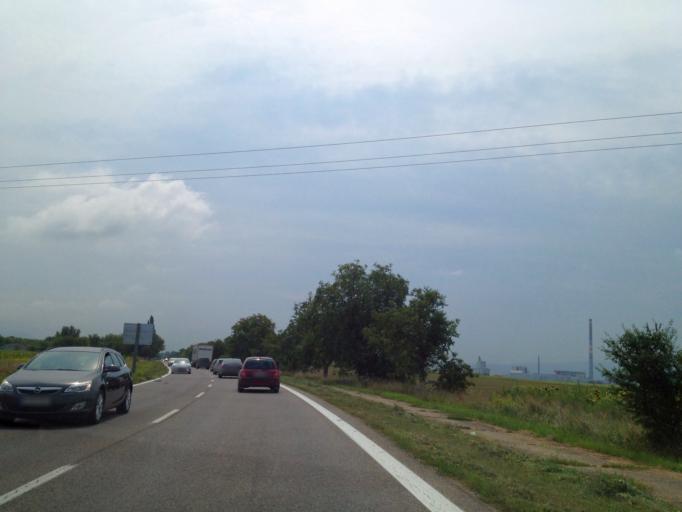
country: SK
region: Nitriansky
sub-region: Okres Nove Zamky
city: Sturovo
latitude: 47.7964
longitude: 18.6927
